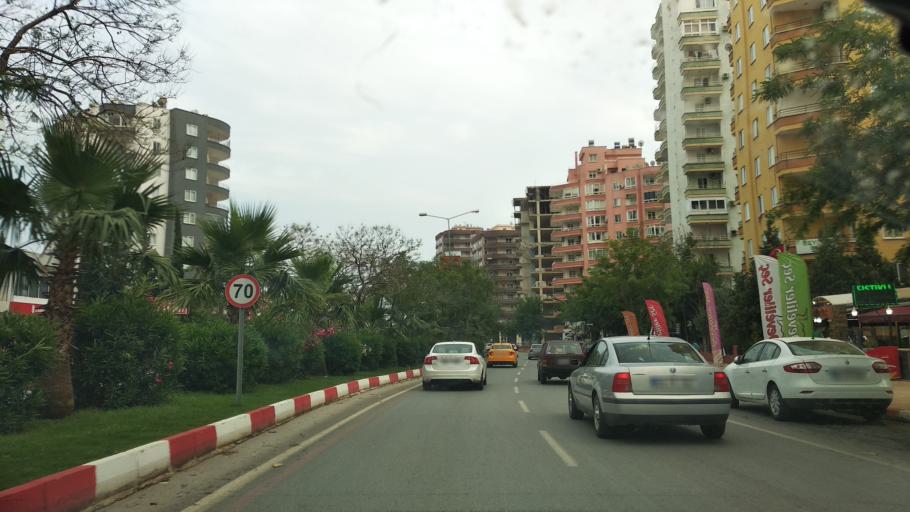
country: TR
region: Mersin
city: Mercin
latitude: 36.7981
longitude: 34.5953
